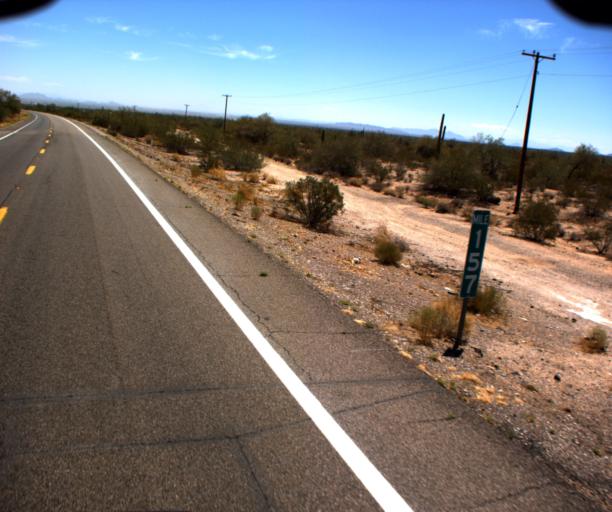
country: US
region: Arizona
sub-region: Pinal County
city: Maricopa
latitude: 32.8429
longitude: -112.1036
